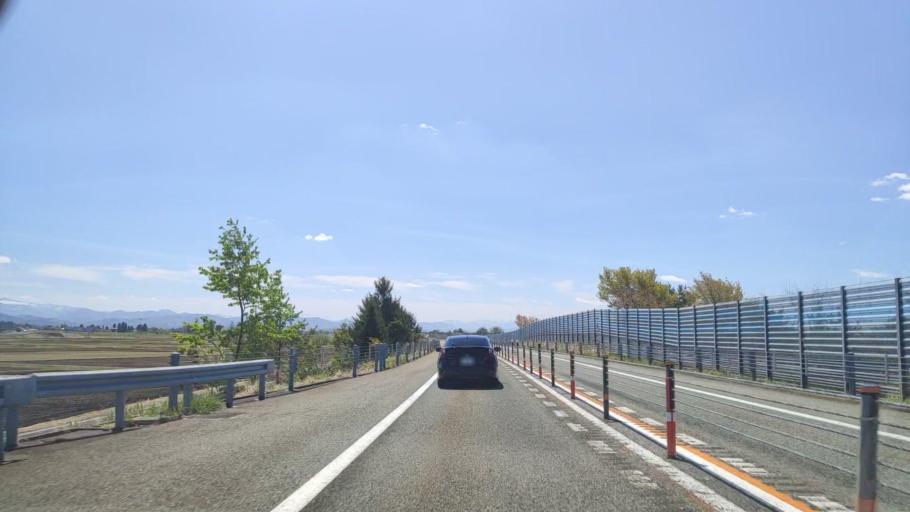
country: JP
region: Akita
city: Omagari
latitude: 39.3814
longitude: 140.4800
